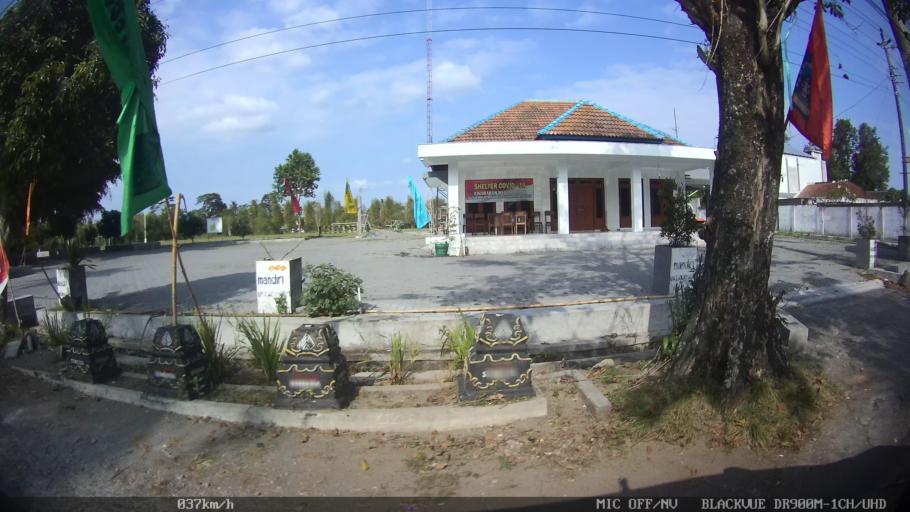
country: ID
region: Daerah Istimewa Yogyakarta
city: Depok
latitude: -7.7313
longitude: 110.4350
